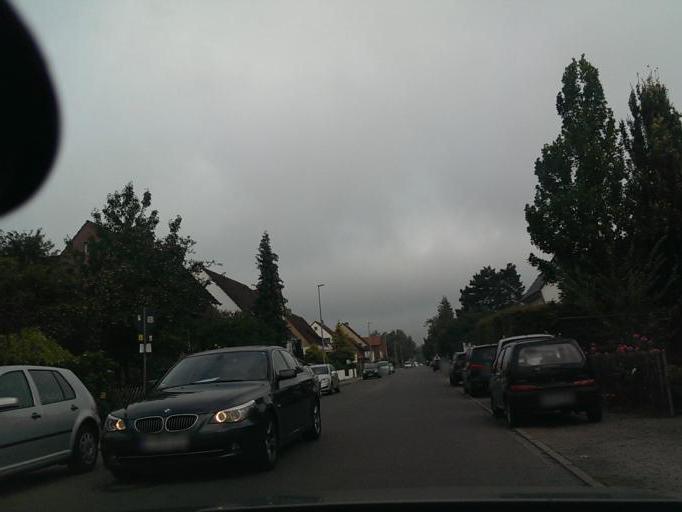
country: DE
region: Lower Saxony
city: Isernhagen Farster Bauerschaft
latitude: 52.4254
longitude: 9.8411
